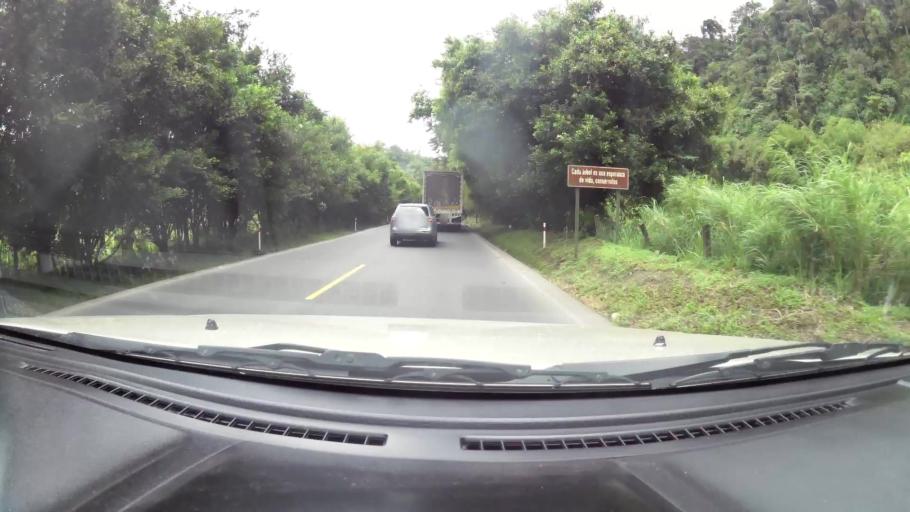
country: EC
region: Santo Domingo de los Tsachilas
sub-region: Canton Santo Domingo de los Colorados
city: Santo Domingo de los Colorados
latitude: -0.2960
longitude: -79.0581
